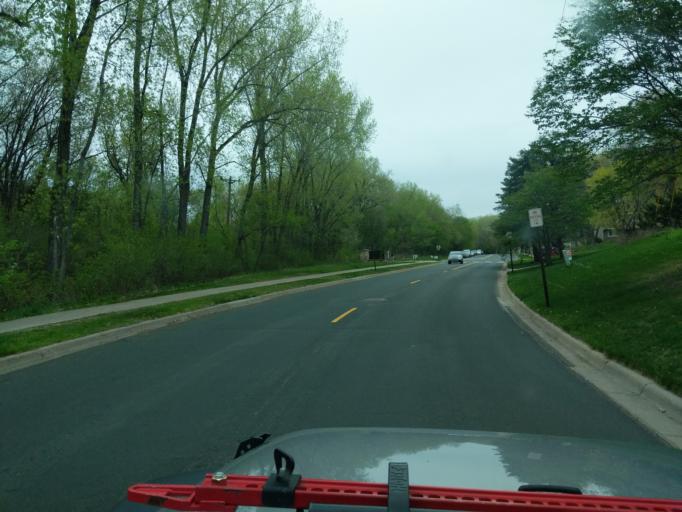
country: US
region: Minnesota
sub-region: Anoka County
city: Coon Rapids
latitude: 45.1490
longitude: -93.3079
